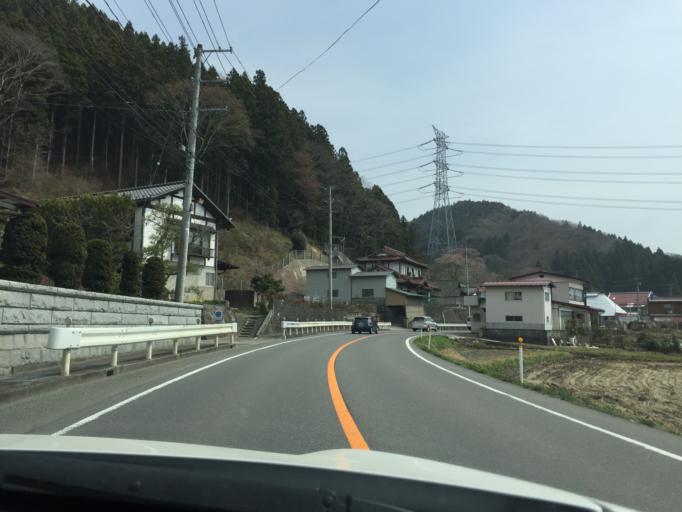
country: JP
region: Fukushima
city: Ishikawa
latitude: 37.1211
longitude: 140.5032
